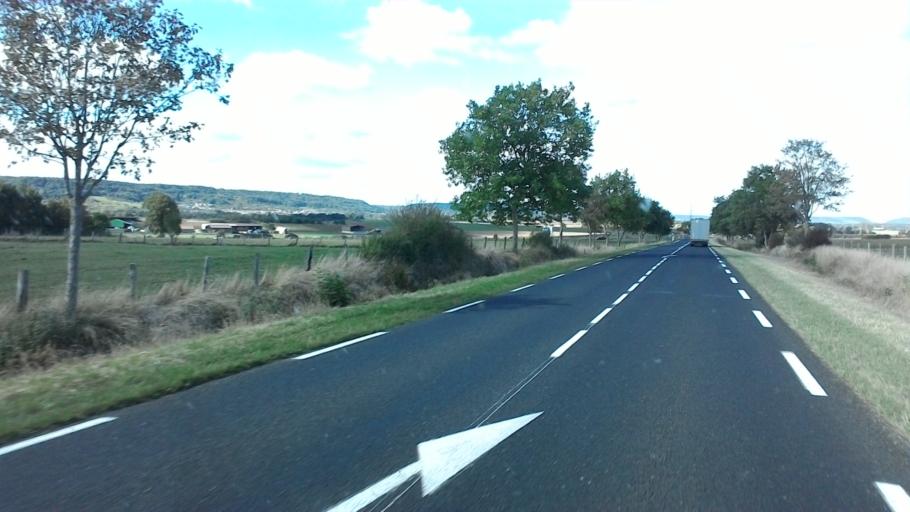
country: FR
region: Lorraine
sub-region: Departement de Meurthe-et-Moselle
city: Colombey-les-Belles
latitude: 48.5568
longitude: 5.8937
